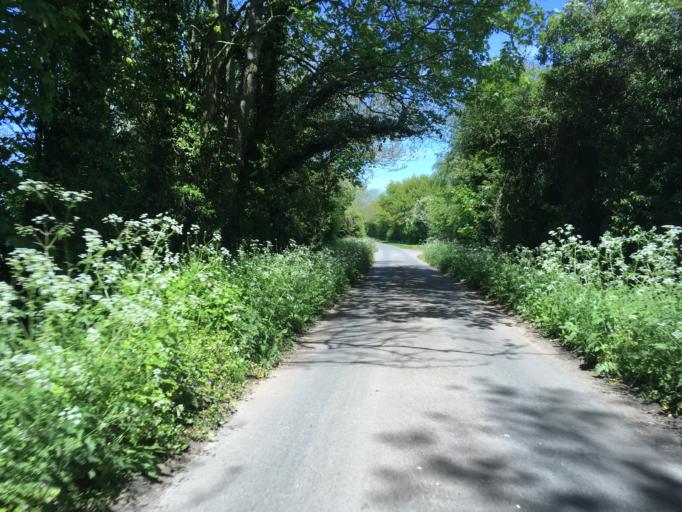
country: GB
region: England
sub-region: Gloucestershire
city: Brimscombe
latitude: 51.7366
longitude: -2.1836
